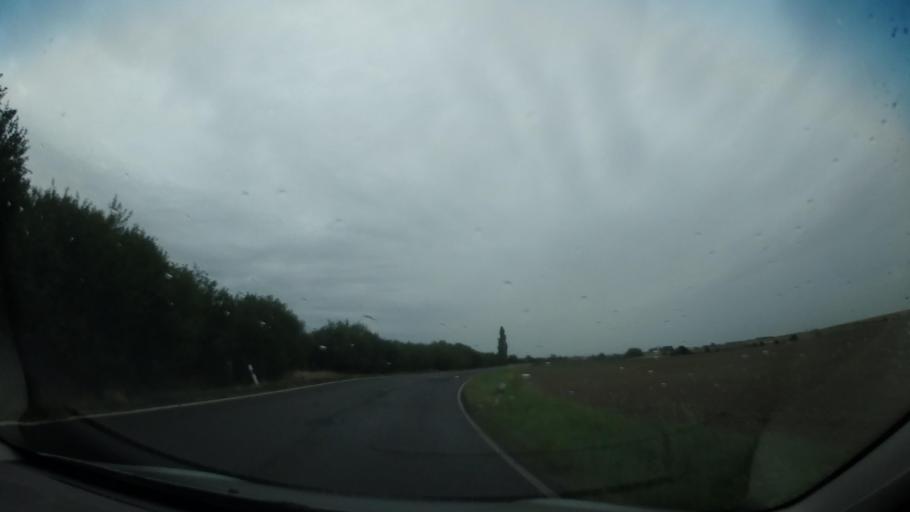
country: CZ
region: Central Bohemia
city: Loucen
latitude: 50.2592
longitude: 15.0250
